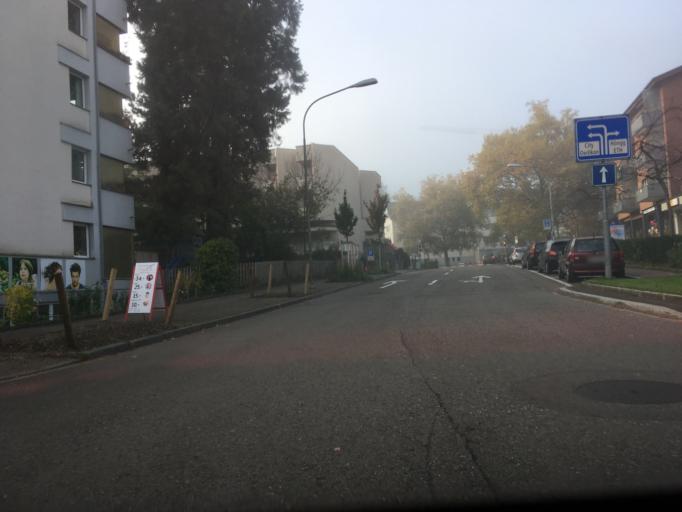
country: CH
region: Zurich
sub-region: Bezirk Zuerich
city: Zuerich (Kreis 11) / Affoltern
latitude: 47.4196
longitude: 8.5083
